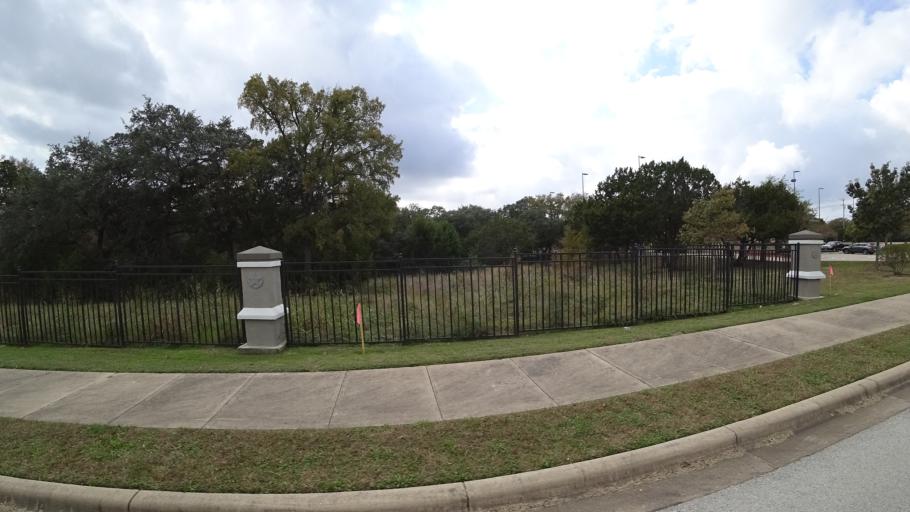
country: US
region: Texas
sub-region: Williamson County
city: Anderson Mill
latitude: 30.4163
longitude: -97.8462
